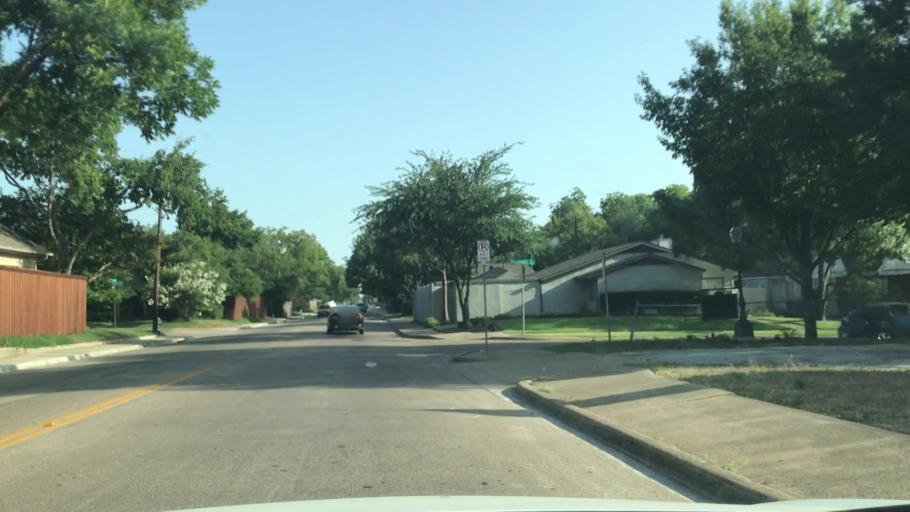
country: US
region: Texas
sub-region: Dallas County
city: Highland Park
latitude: 32.8285
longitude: -96.7702
